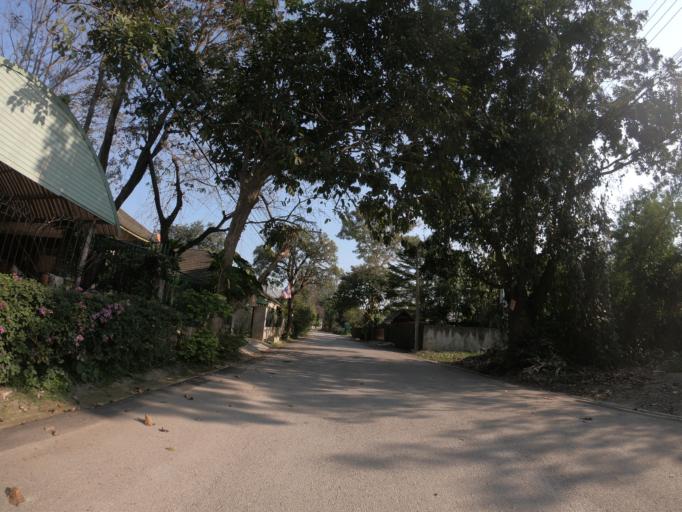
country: TH
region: Chiang Mai
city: San Sai
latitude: 18.8326
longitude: 99.0055
